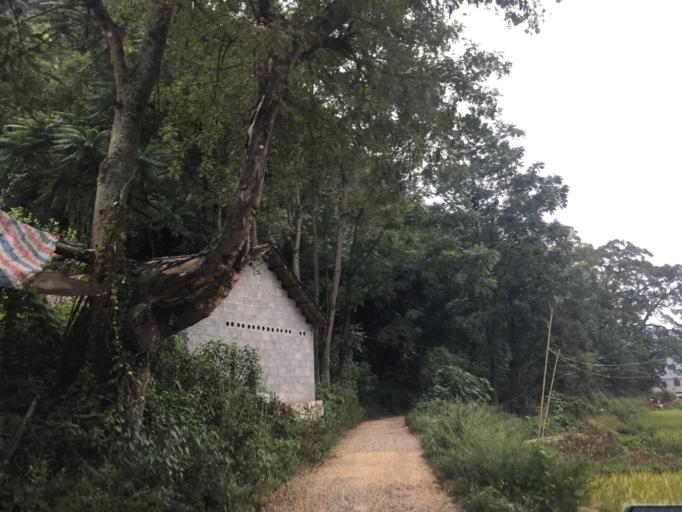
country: CN
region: Guangxi Zhuangzu Zizhiqu
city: Xinzhou
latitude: 25.4986
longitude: 105.6485
